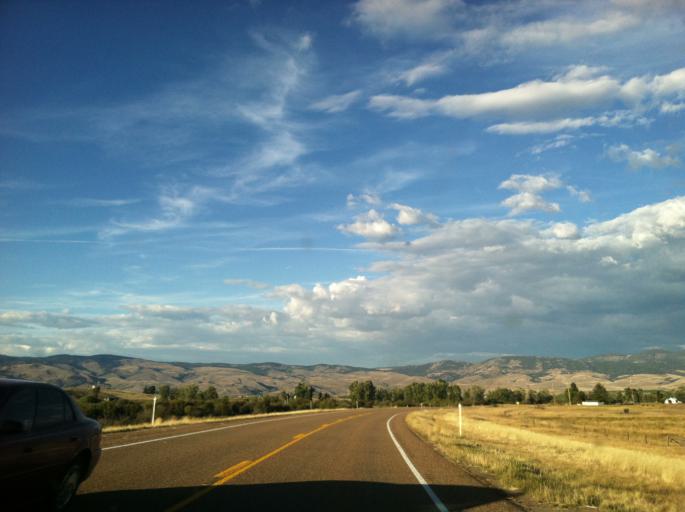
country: US
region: Montana
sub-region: Granite County
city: Philipsburg
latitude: 46.6082
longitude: -113.1837
